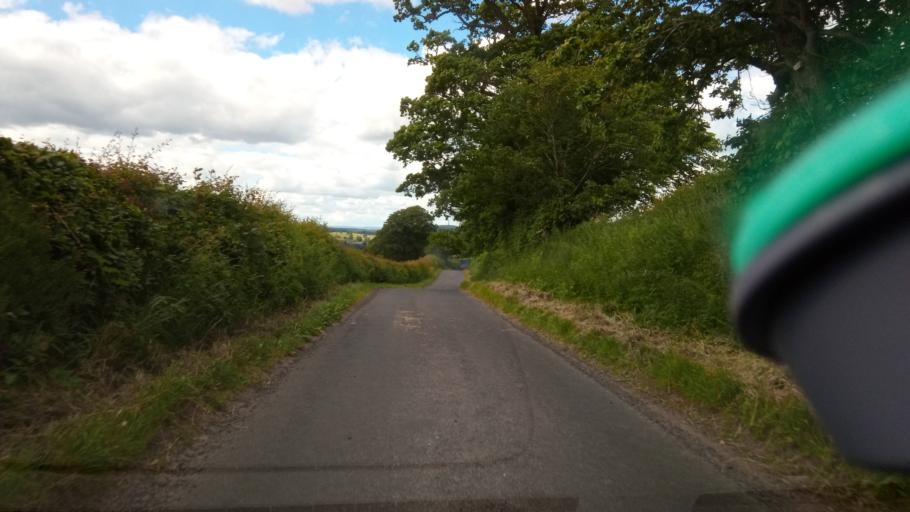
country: GB
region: Scotland
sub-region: The Scottish Borders
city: Jedburgh
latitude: 55.4616
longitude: -2.5476
